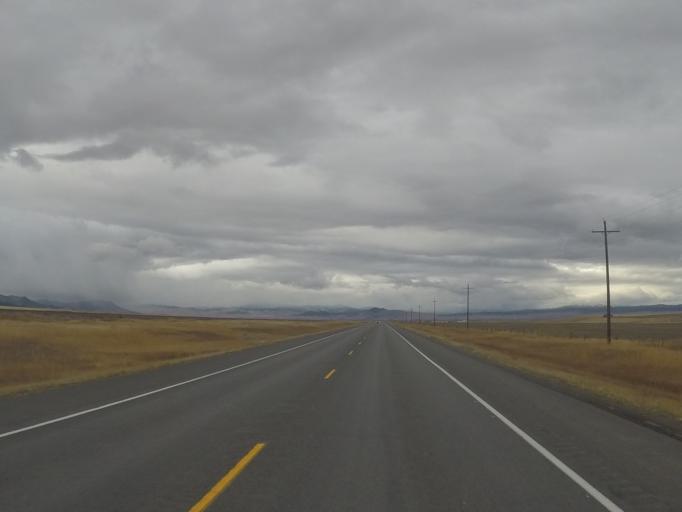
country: US
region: Montana
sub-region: Lewis and Clark County
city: East Helena
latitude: 46.5750
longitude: -111.8330
